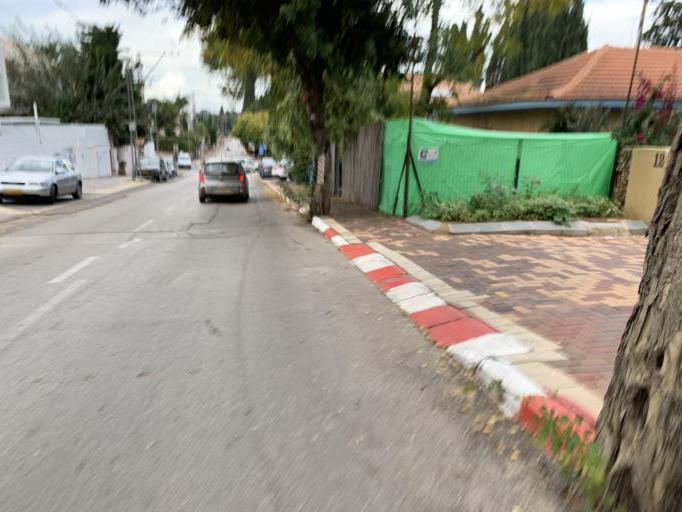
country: IL
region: Central District
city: Hod HaSharon
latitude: 32.1581
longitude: 34.8870
